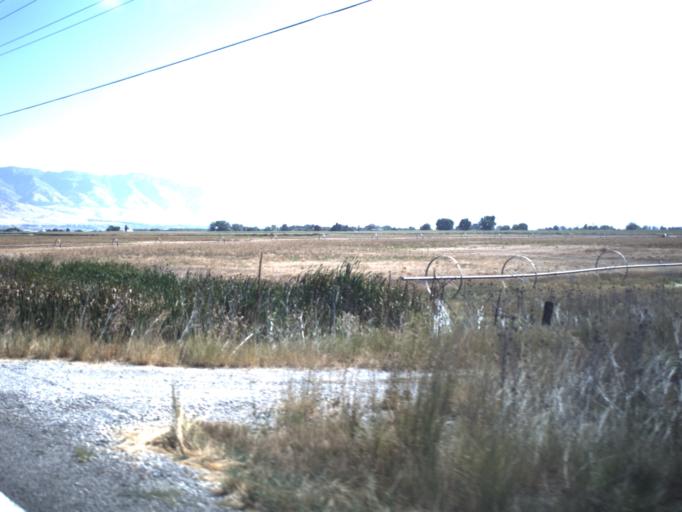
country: US
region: Utah
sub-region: Cache County
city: Benson
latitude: 41.8450
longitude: -111.9213
